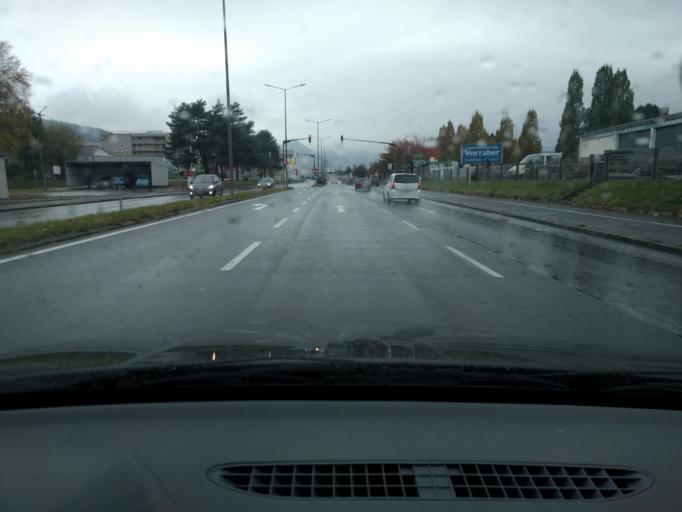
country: AT
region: Styria
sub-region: Politischer Bezirk Leoben
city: Leoben
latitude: 47.3829
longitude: 15.1118
